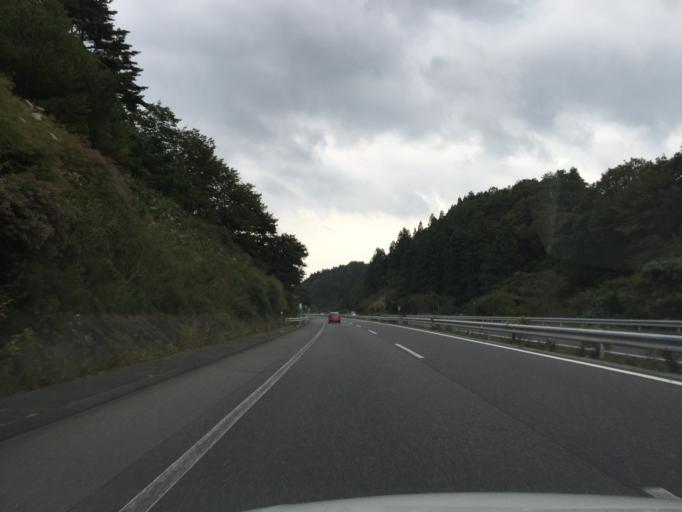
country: JP
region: Fukushima
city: Iwaki
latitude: 37.1859
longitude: 140.7101
